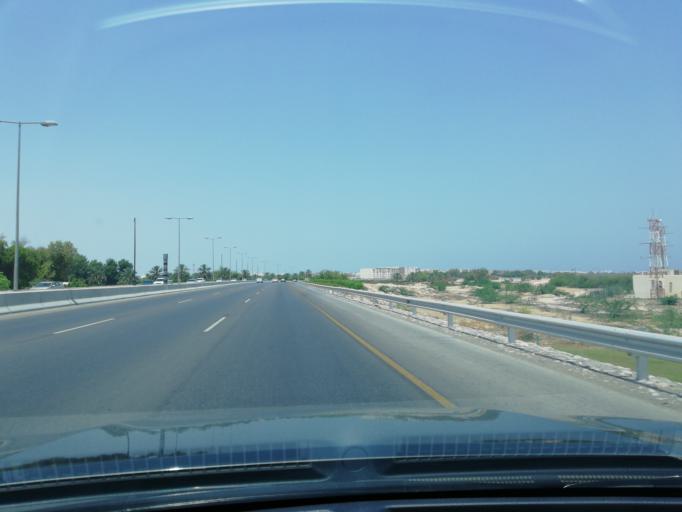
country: OM
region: Muhafazat Masqat
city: As Sib al Jadidah
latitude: 23.5892
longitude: 58.2540
